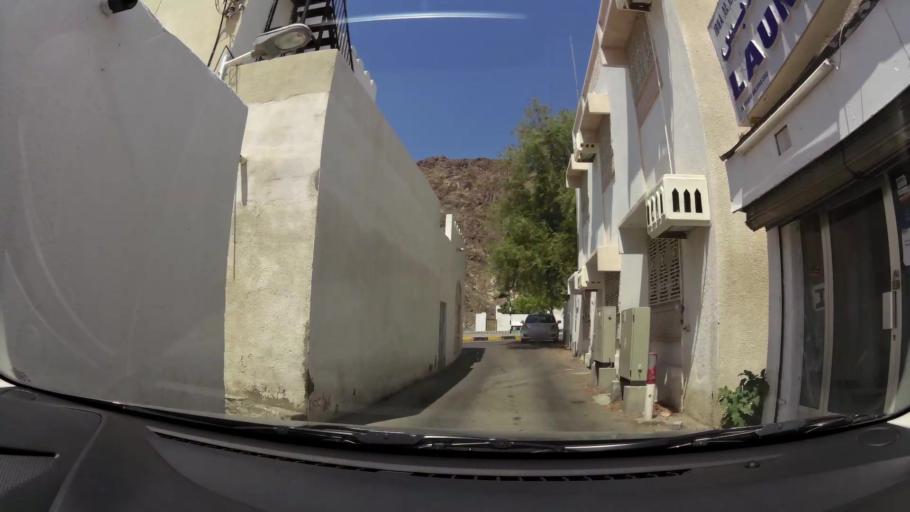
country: OM
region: Muhafazat Masqat
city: Muscat
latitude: 23.5934
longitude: 58.5978
